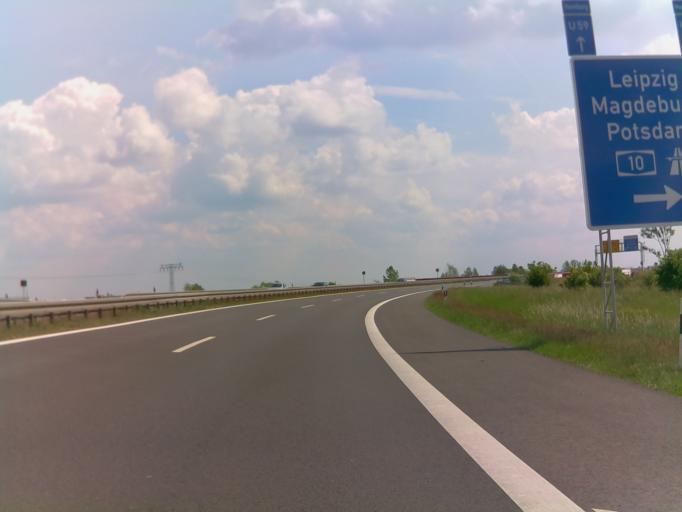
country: DE
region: Brandenburg
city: Wustermark
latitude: 52.5563
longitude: 12.9612
